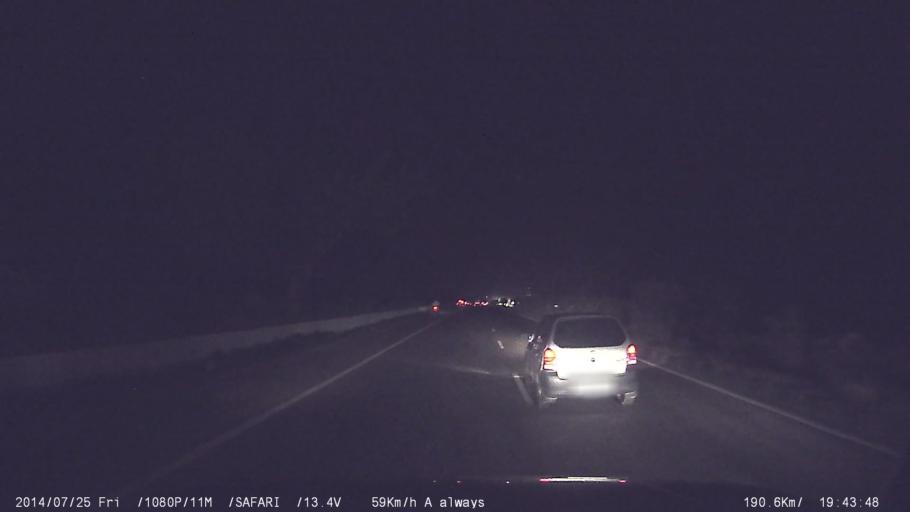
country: IN
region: Tamil Nadu
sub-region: Salem
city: Omalur
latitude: 11.7005
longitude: 78.1047
